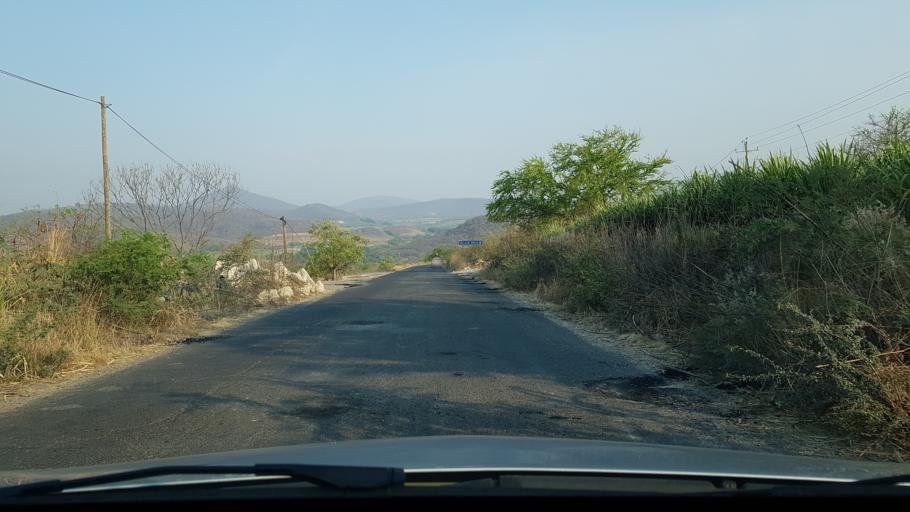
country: MX
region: Morelos
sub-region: Tepalcingo
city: Zacapalco
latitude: 18.6299
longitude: -99.0091
